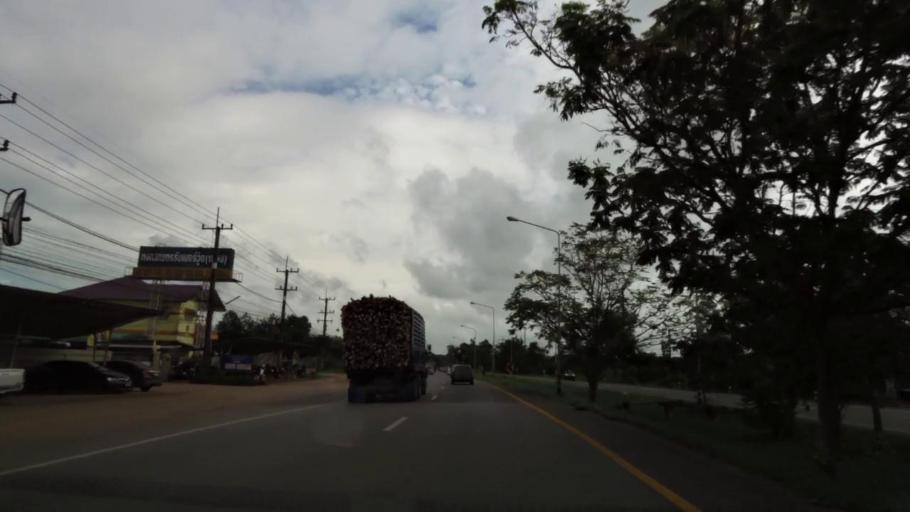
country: TH
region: Chanthaburi
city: Na Yai Am
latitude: 12.7307
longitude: 101.9154
